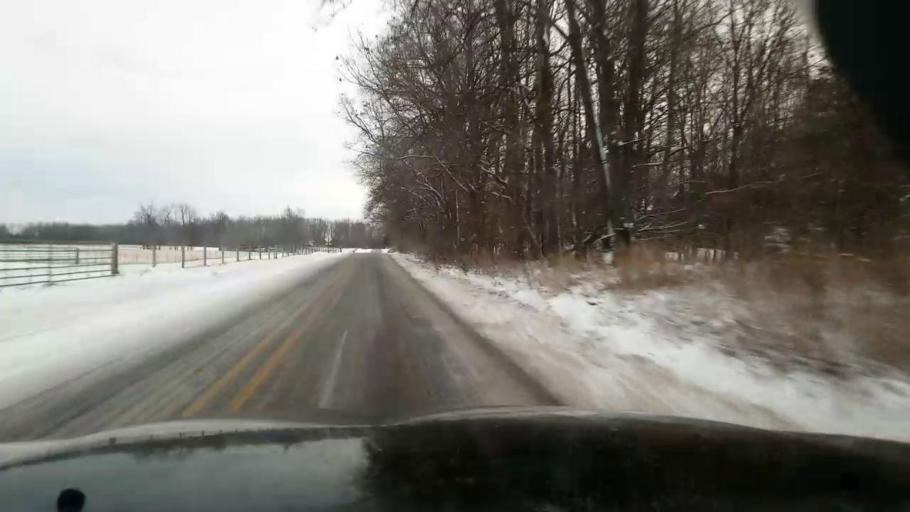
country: US
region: Michigan
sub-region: Jackson County
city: Vandercook Lake
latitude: 42.0928
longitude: -84.4657
